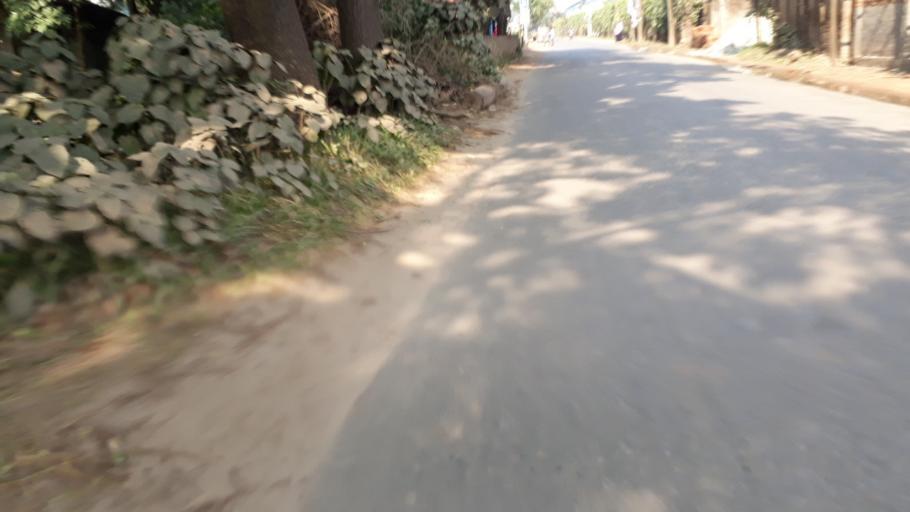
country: BD
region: Dhaka
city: Tungi
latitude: 23.8624
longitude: 90.3109
